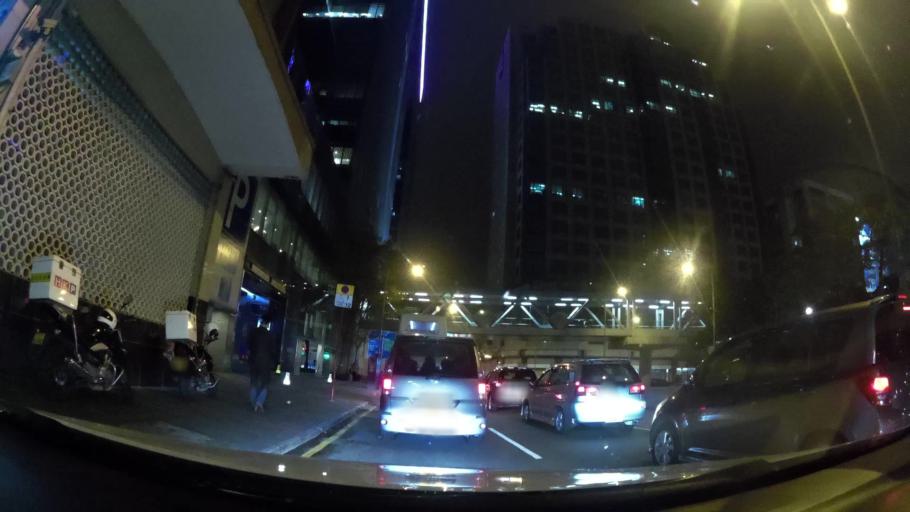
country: HK
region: Kowloon City
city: Kowloon
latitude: 22.3080
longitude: 114.2230
